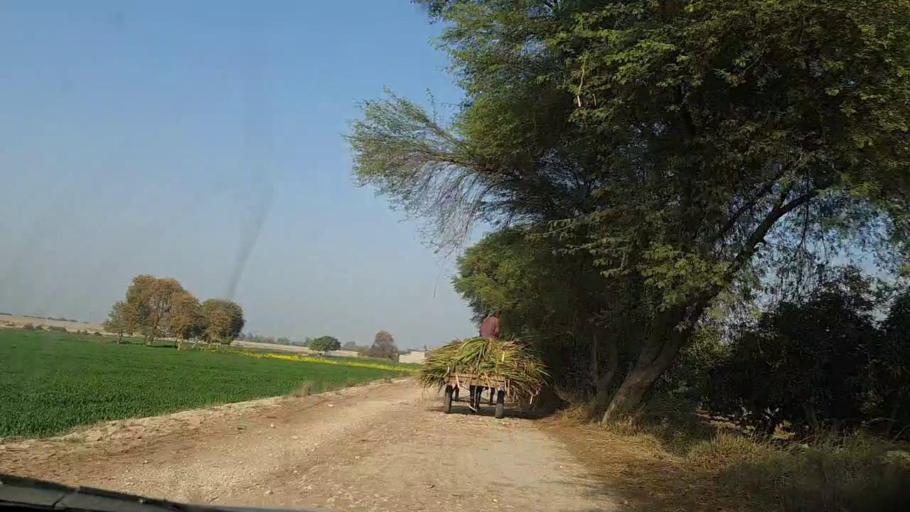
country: PK
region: Sindh
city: Moro
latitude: 26.7983
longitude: 67.9448
